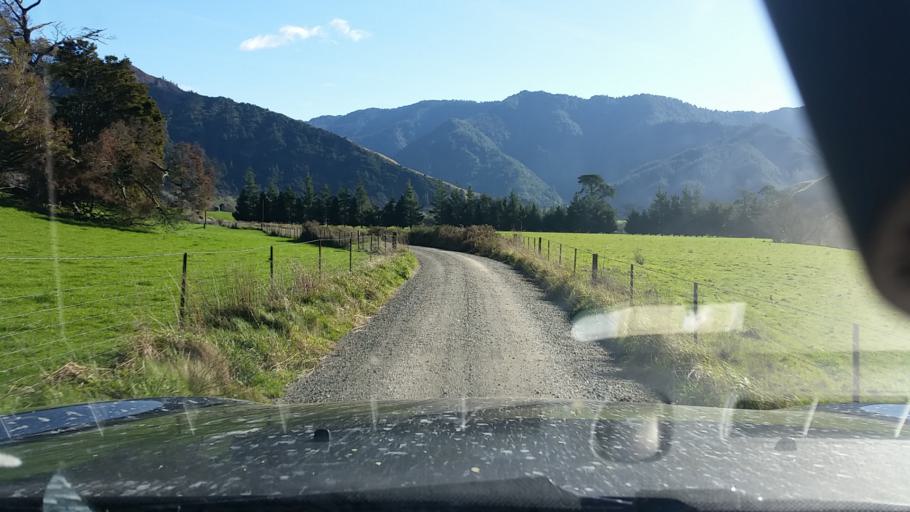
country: NZ
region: Marlborough
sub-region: Marlborough District
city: Picton
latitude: -41.3345
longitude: 173.7778
